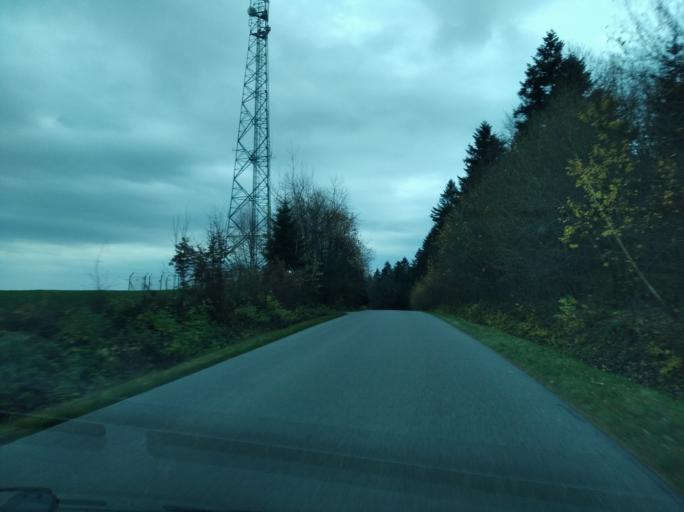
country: PL
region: Subcarpathian Voivodeship
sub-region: Powiat ropczycko-sedziszowski
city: Zagorzyce
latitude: 49.9565
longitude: 21.6937
